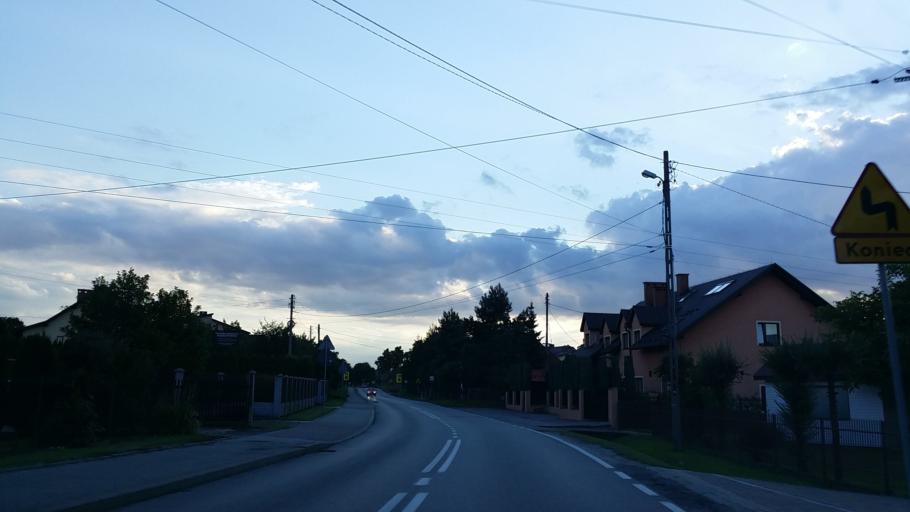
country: PL
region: Lesser Poland Voivodeship
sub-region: Powiat oswiecimski
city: Przeciszow
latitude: 49.9988
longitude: 19.3690
